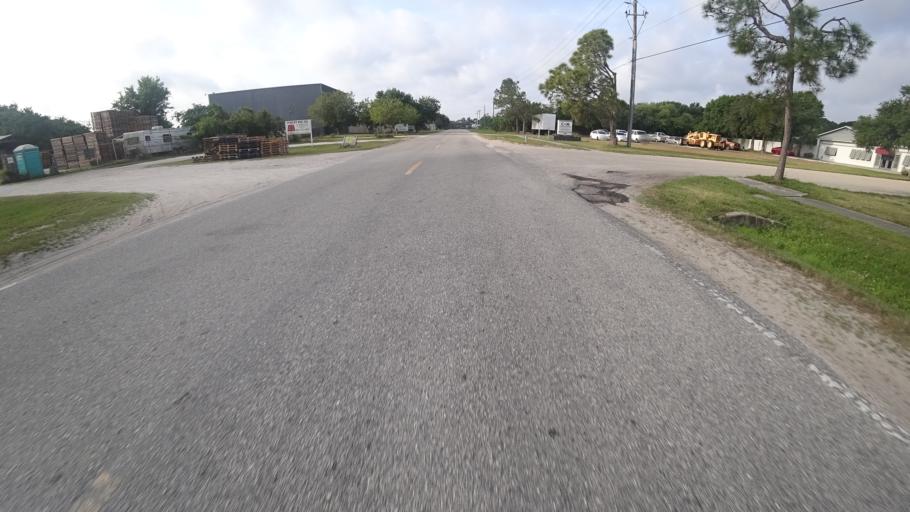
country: US
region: Florida
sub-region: Manatee County
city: Whitfield
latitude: 27.4208
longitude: -82.5219
